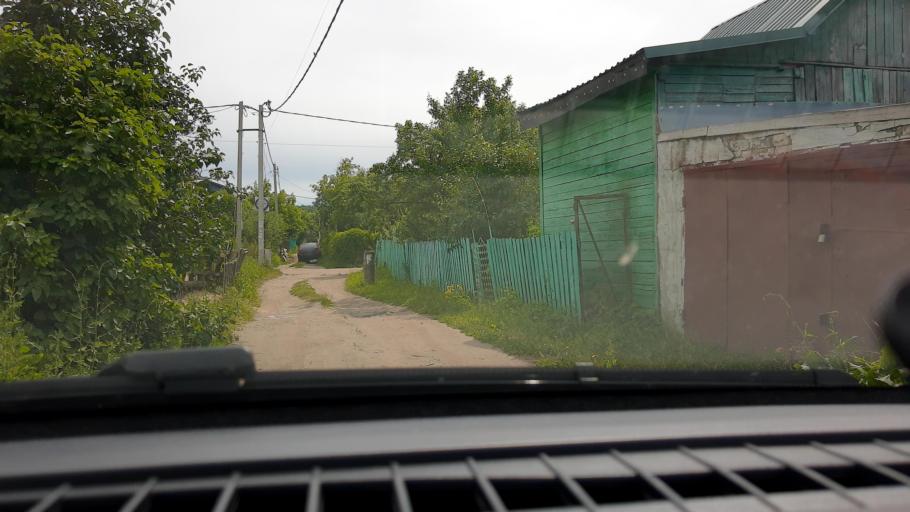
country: RU
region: Nizjnij Novgorod
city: Nizhniy Novgorod
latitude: 56.2683
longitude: 43.9542
